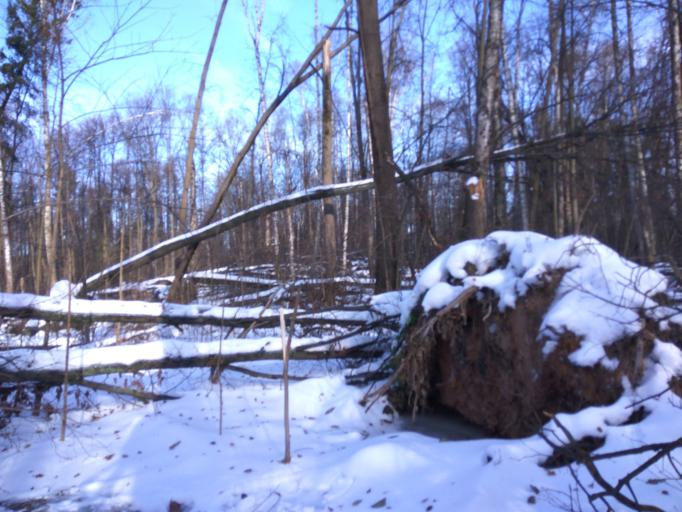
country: RU
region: Moscow
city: Babushkin
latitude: 55.8496
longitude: 37.7441
